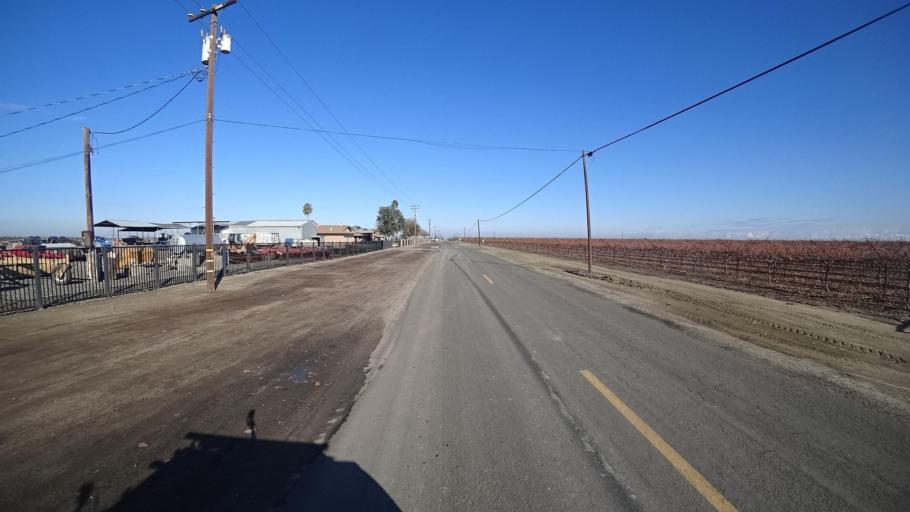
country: US
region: California
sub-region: Kern County
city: McFarland
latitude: 35.7002
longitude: -119.2764
